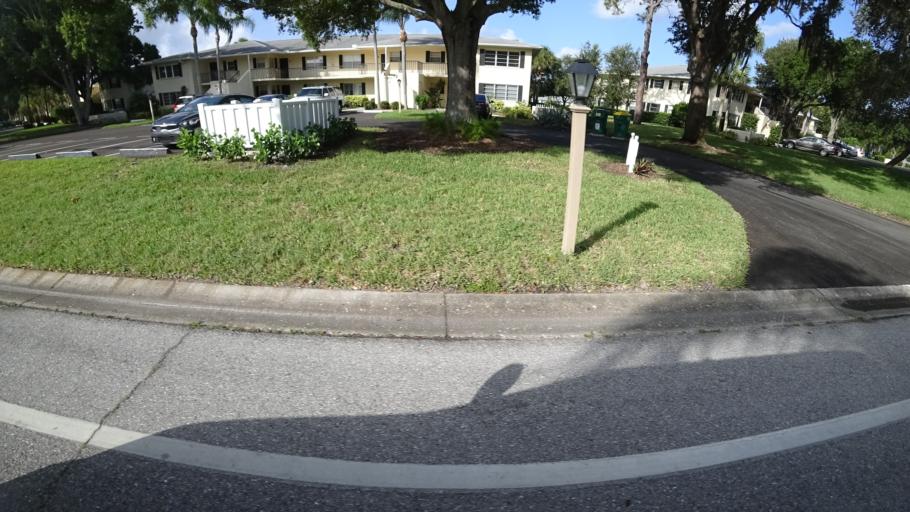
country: US
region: Florida
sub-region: Sarasota County
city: Desoto Lakes
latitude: 27.4177
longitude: -82.4950
